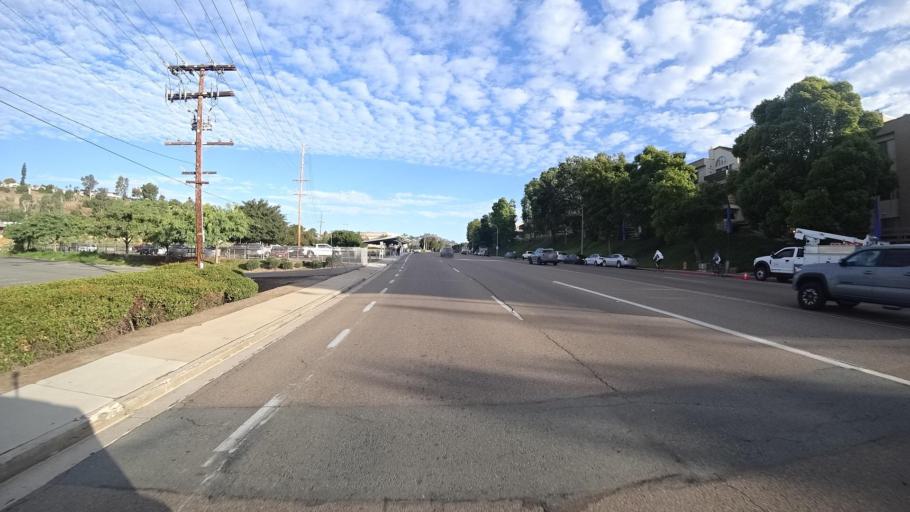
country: US
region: California
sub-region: San Diego County
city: Casa de Oro-Mount Helix
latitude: 32.7369
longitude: -116.9718
